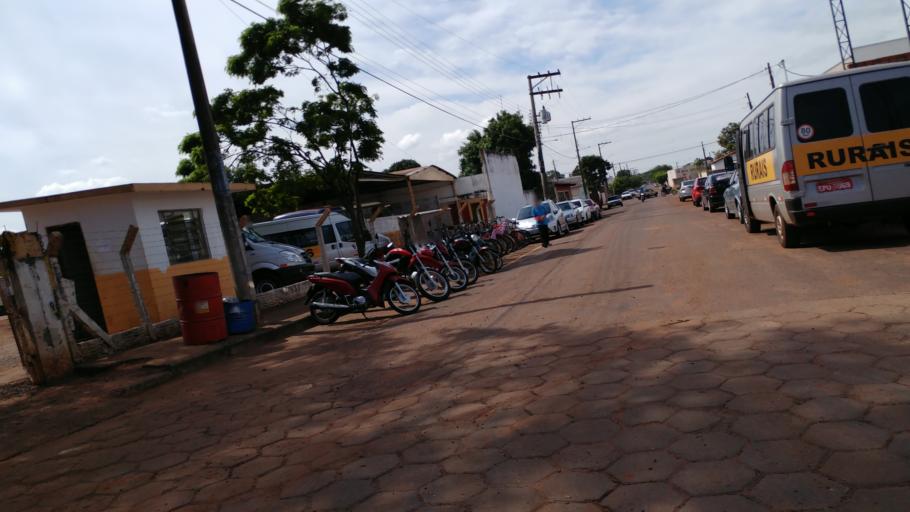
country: BR
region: Sao Paulo
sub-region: Paraguacu Paulista
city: Paraguacu Paulista
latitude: -22.4287
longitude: -50.5858
